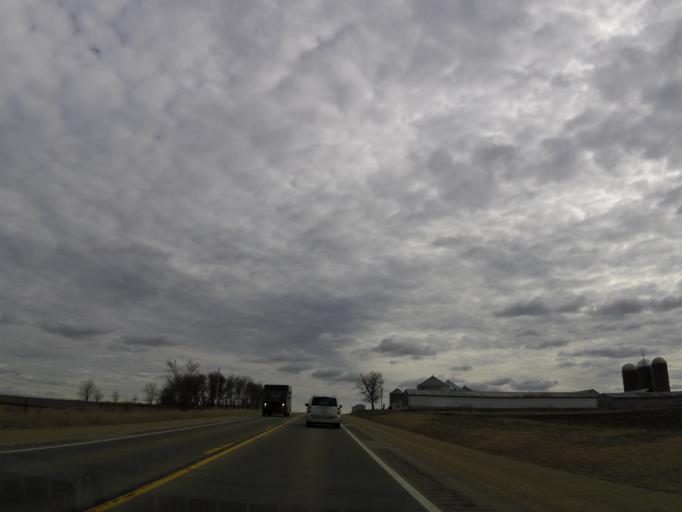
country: US
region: Iowa
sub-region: Chickasaw County
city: New Hampton
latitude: 43.1792
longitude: -92.2986
